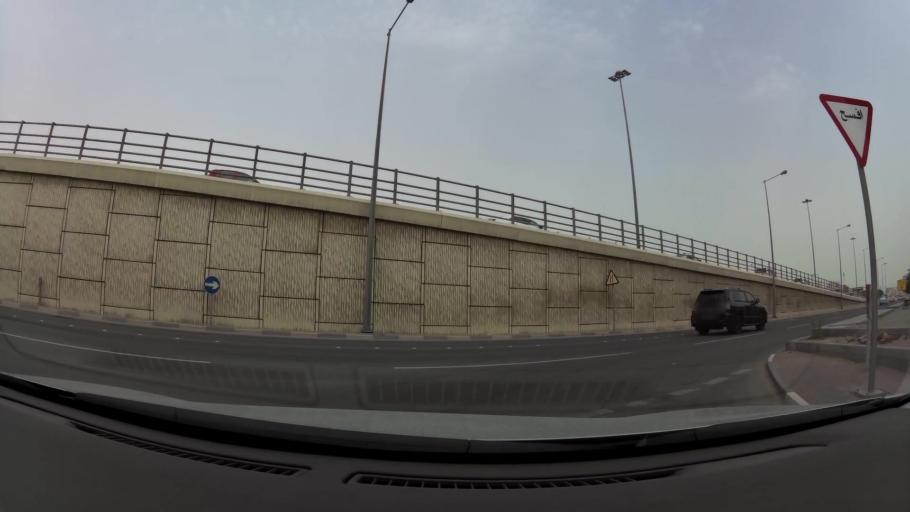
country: QA
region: Baladiyat ad Dawhah
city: Doha
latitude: 25.2649
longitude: 51.4990
